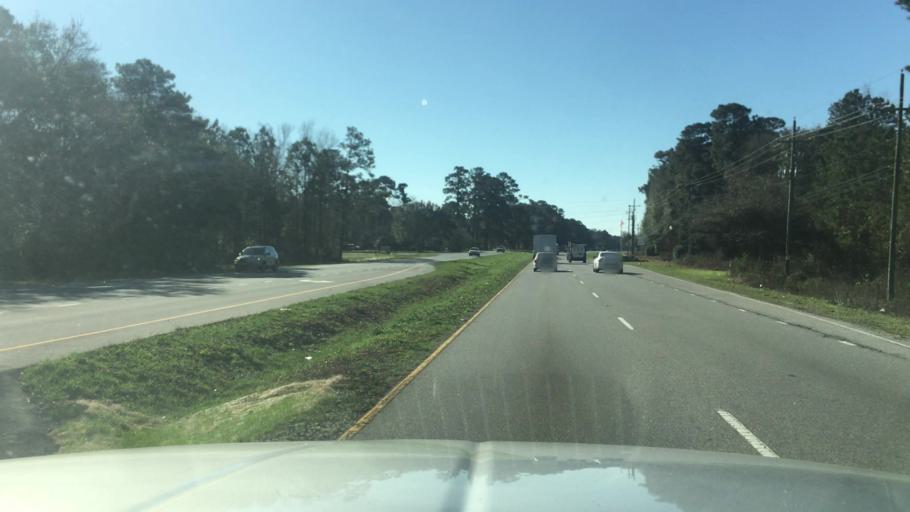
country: US
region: North Carolina
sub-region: New Hanover County
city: Sea Breeze
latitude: 34.0961
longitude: -77.8983
